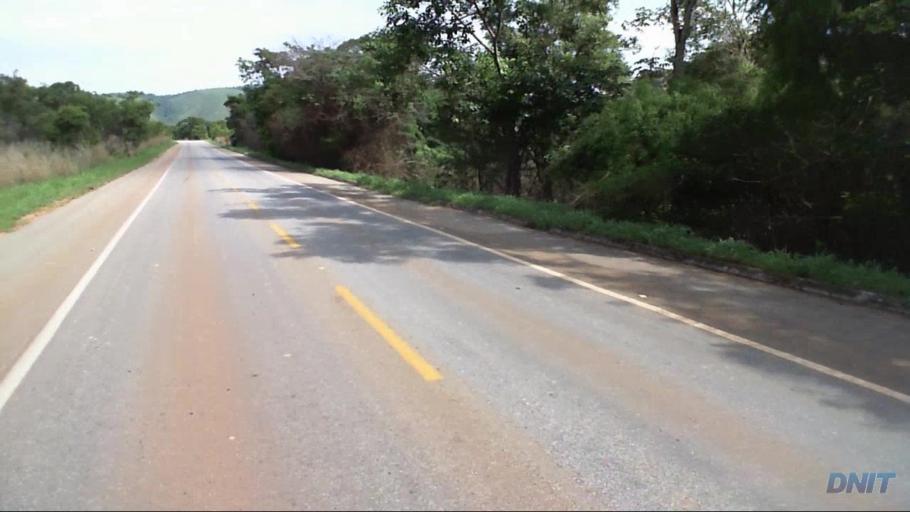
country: BR
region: Goias
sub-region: Barro Alto
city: Barro Alto
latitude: -15.1609
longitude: -48.8005
